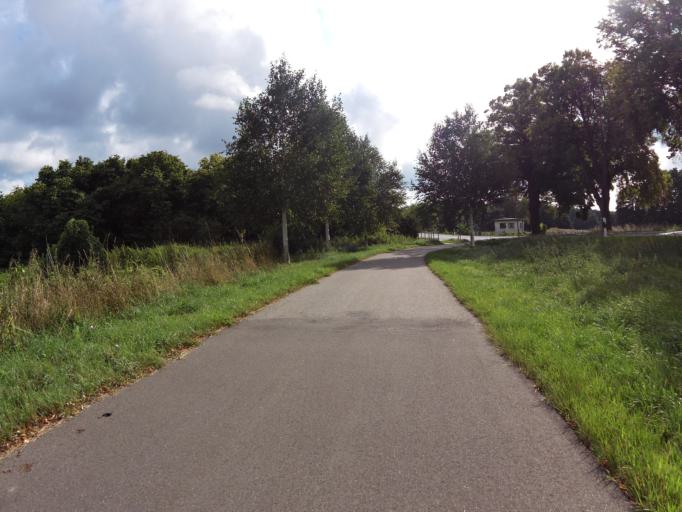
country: DE
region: Mecklenburg-Vorpommern
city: Seebad Bansin
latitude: 53.9638
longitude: 14.0633
